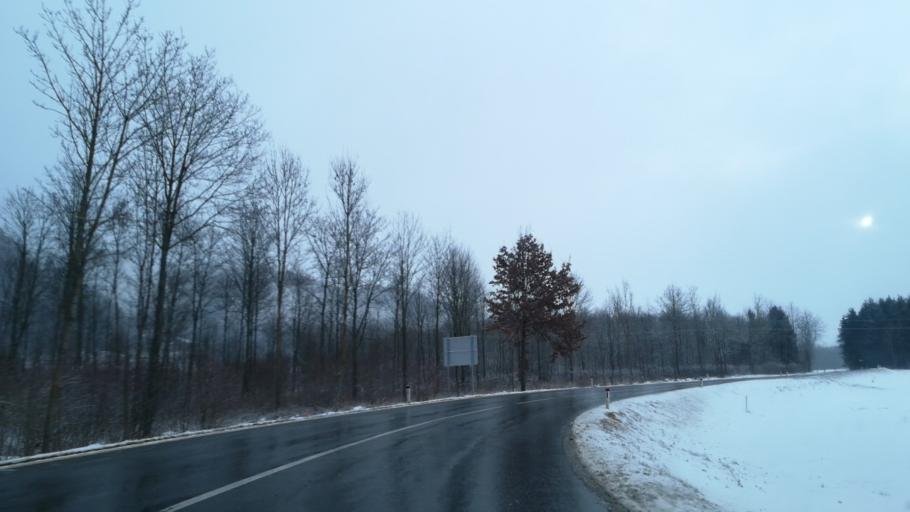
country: AT
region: Styria
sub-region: Politischer Bezirk Murtal
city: Poels
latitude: 47.2239
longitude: 14.5951
